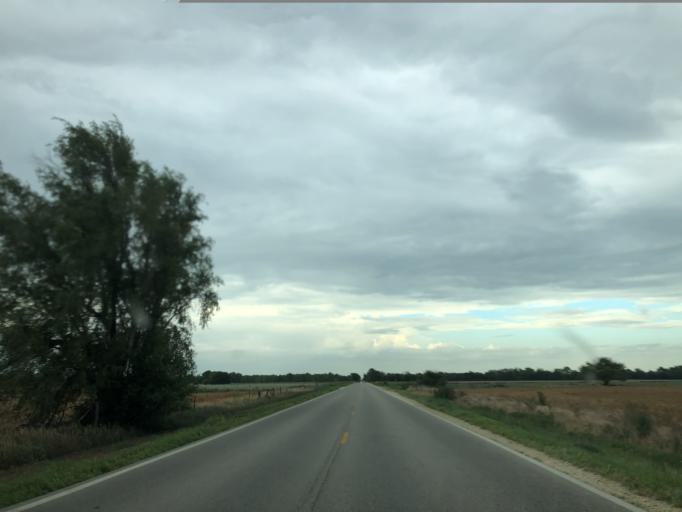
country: US
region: Kansas
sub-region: Reno County
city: Nickerson
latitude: 38.1449
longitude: -98.1357
